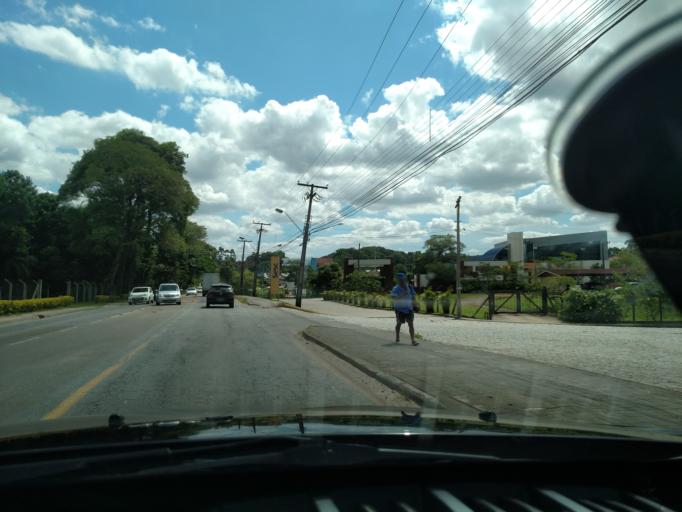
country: BR
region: Santa Catarina
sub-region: Blumenau
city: Blumenau
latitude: -26.8730
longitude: -49.1022
